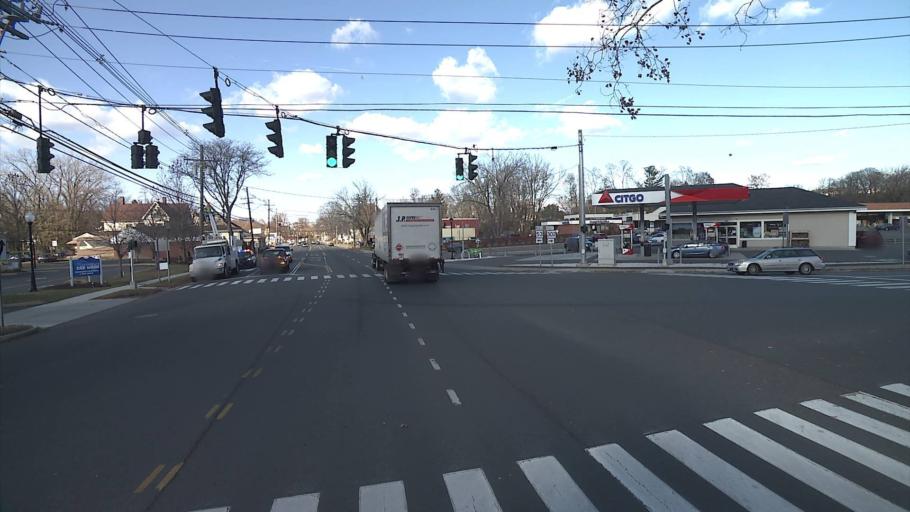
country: US
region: Connecticut
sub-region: Fairfield County
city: Bethel
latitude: 41.3744
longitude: -73.4241
